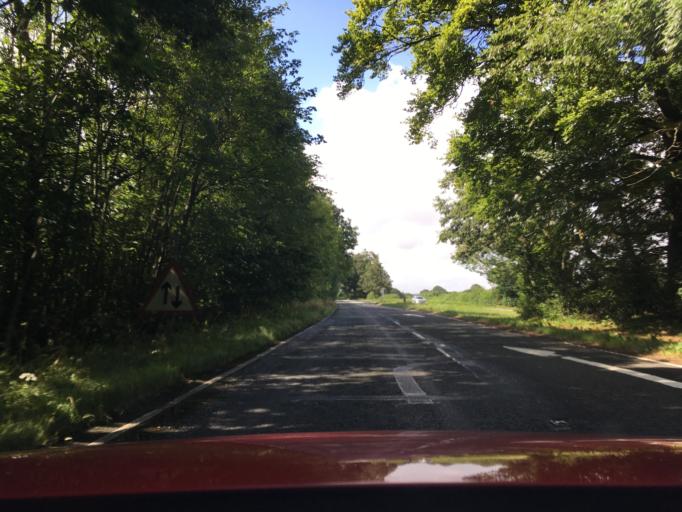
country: GB
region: England
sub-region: Hampshire
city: Basingstoke
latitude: 51.2205
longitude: -1.1657
